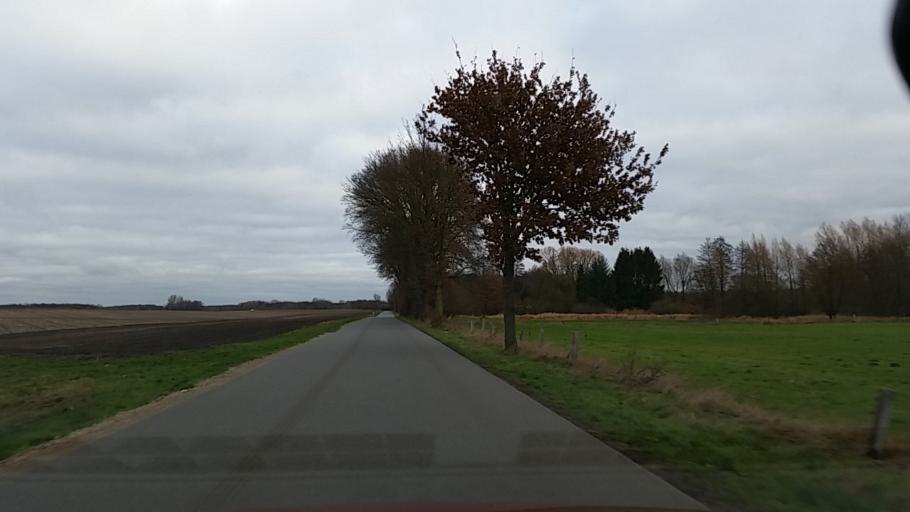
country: DE
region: Lower Saxony
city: Luder
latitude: 52.8153
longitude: 10.6679
